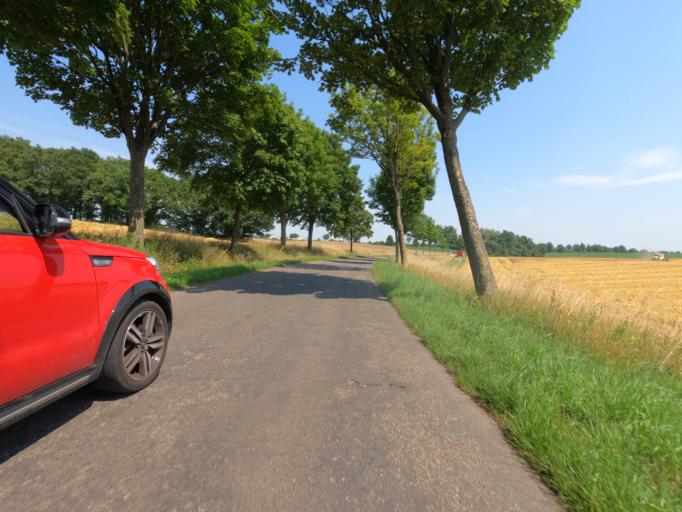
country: DE
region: North Rhine-Westphalia
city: Geilenkirchen
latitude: 50.9691
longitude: 6.0827
